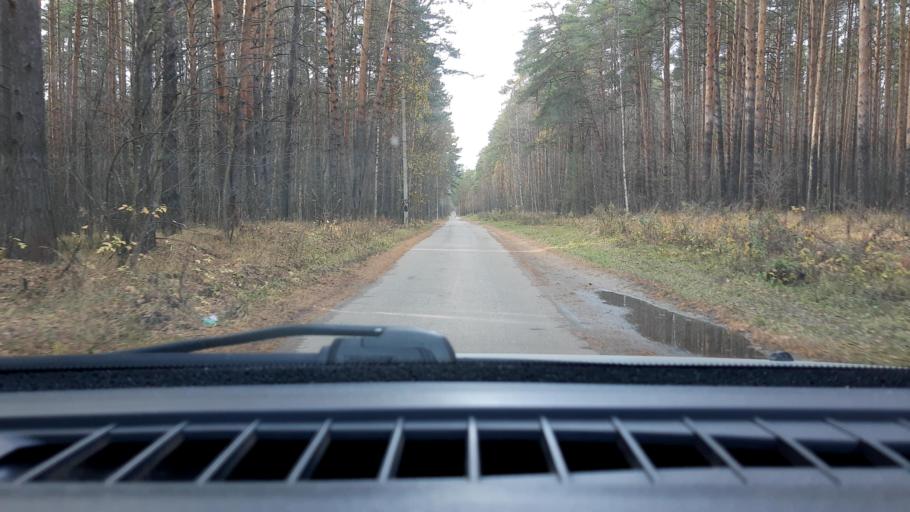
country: RU
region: Nizjnij Novgorod
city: Kstovo
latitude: 56.1677
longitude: 44.1151
